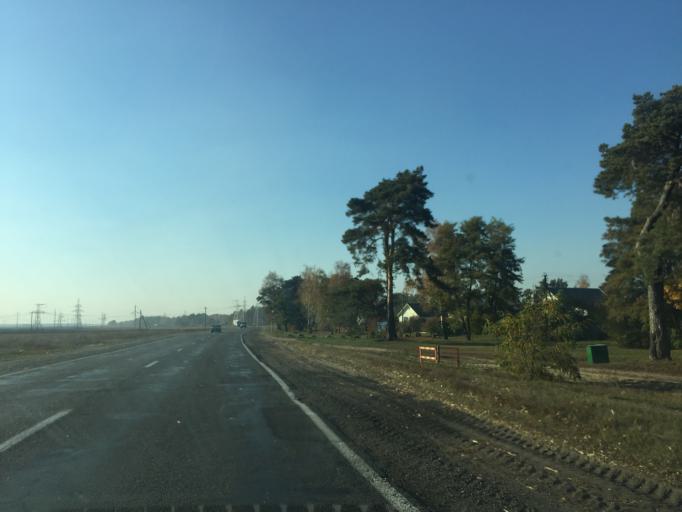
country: BY
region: Gomel
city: Dobrush
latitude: 52.3847
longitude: 31.2981
